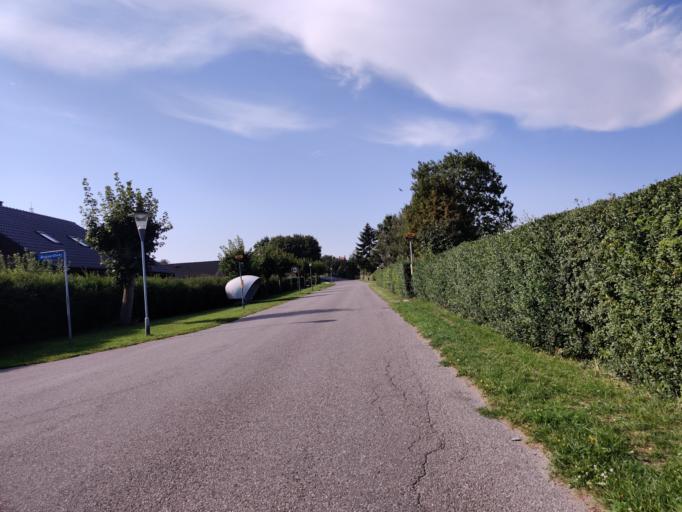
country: DK
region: Zealand
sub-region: Guldborgsund Kommune
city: Nykobing Falster
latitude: 54.7072
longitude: 11.9290
